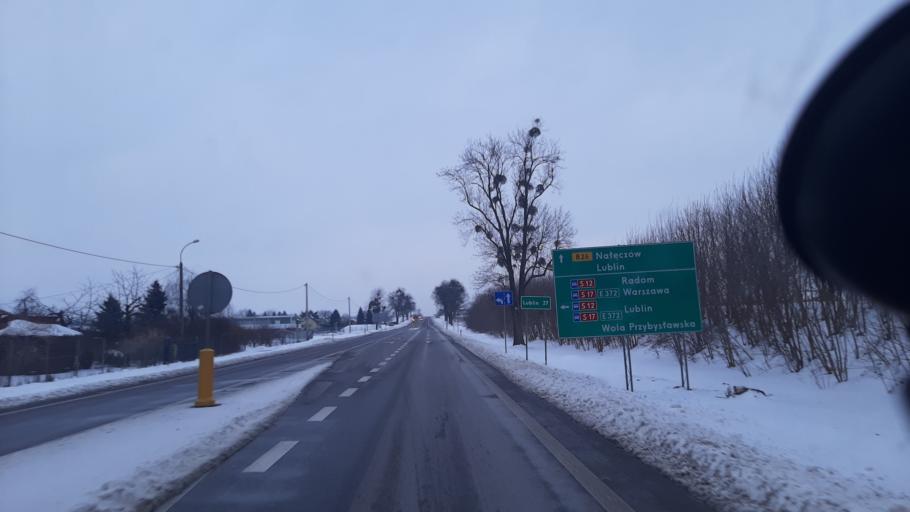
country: PL
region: Lublin Voivodeship
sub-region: Powiat pulawski
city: Markuszow
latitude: 51.3714
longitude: 22.2737
